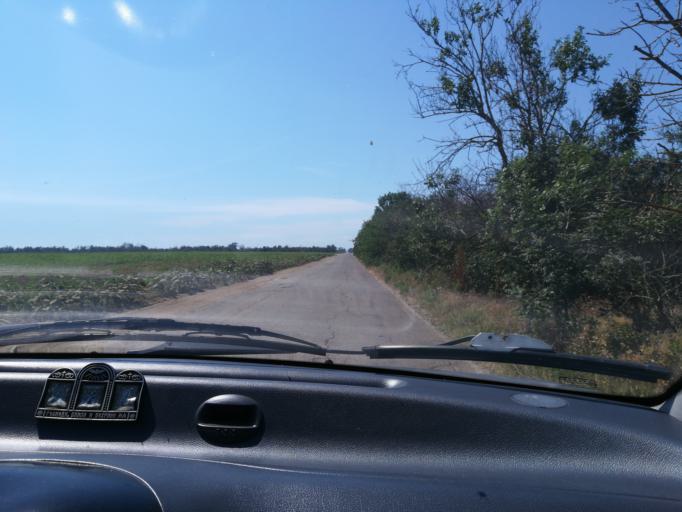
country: RU
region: Krasnodarskiy
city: Blagovetschenskaya
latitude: 45.0595
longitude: 37.0957
